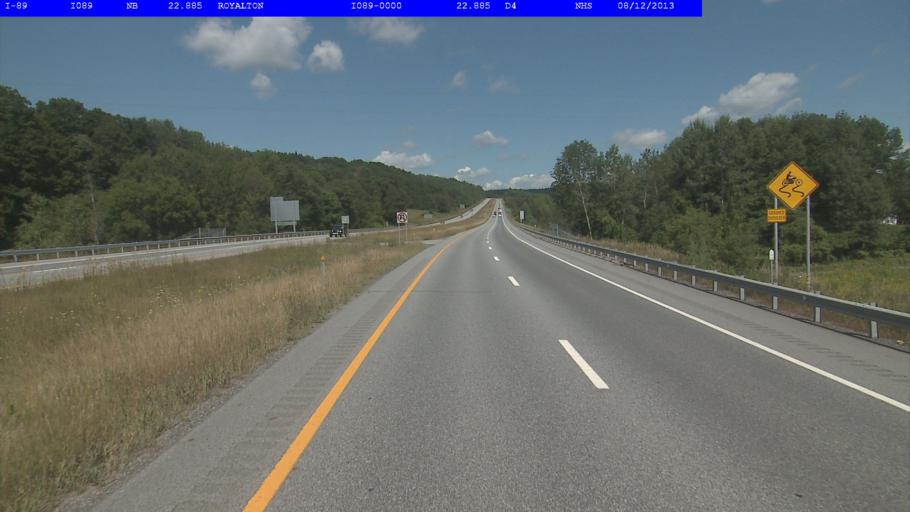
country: US
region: Vermont
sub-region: Orange County
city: Randolph
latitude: 43.8342
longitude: -72.5898
